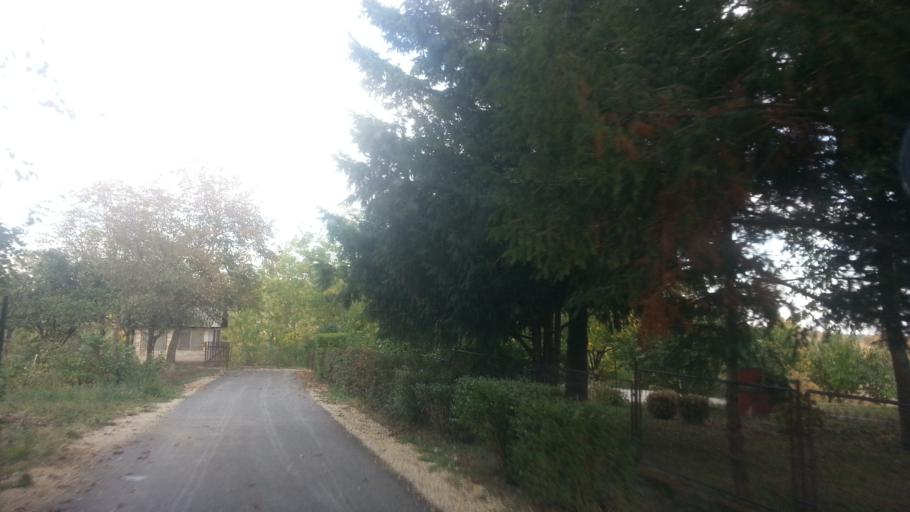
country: RS
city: Belegis
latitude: 45.0270
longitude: 20.3522
